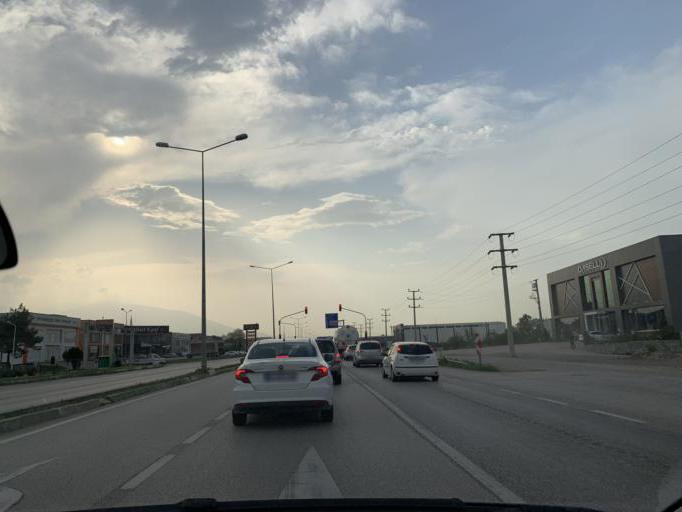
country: TR
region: Bursa
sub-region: Inegoel
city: Inegol
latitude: 40.0744
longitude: 29.5356
